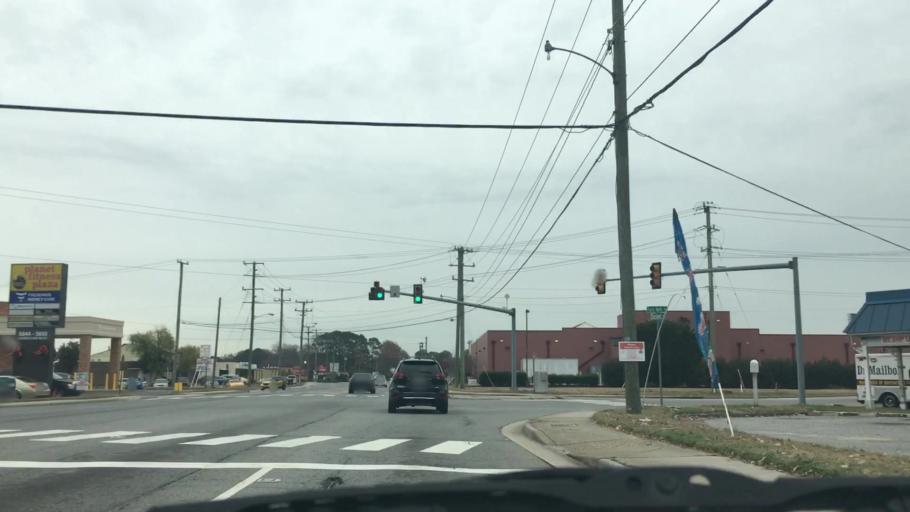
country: US
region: Virginia
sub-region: City of Portsmouth
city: Portsmouth Heights
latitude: 36.8635
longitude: -76.3954
